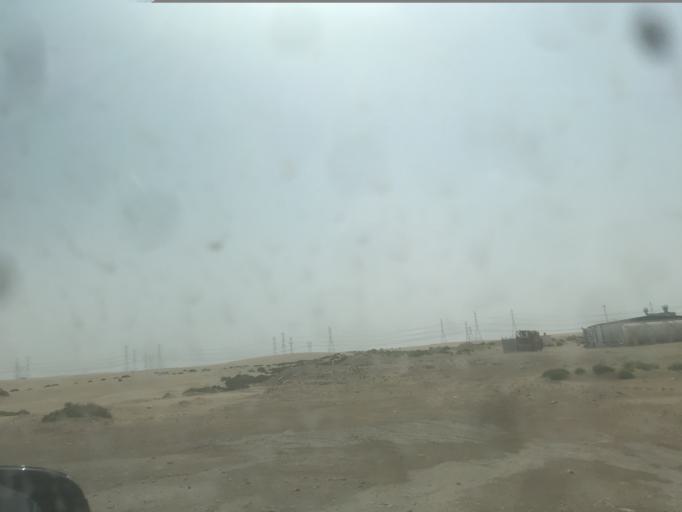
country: SA
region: Eastern Province
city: Abqaiq
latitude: 25.9175
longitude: 49.8535
